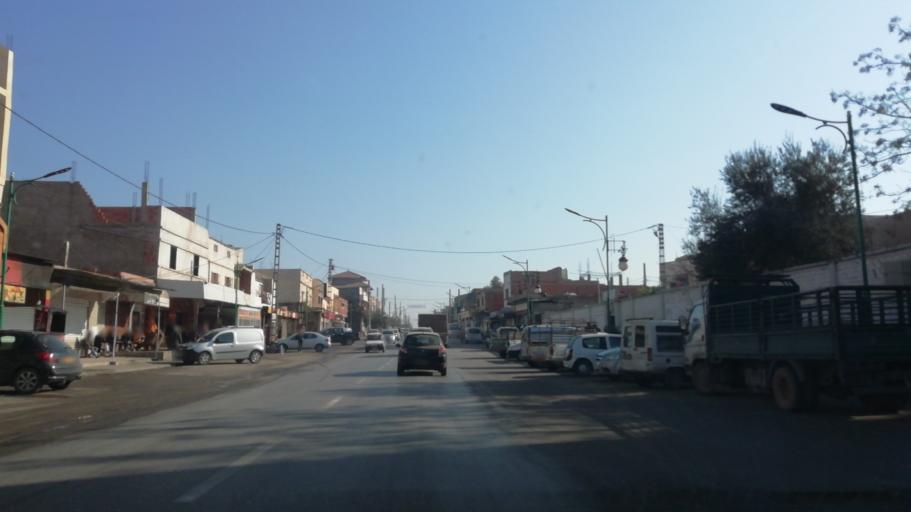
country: DZ
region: Relizane
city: Relizane
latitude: 35.7333
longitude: 0.4563
